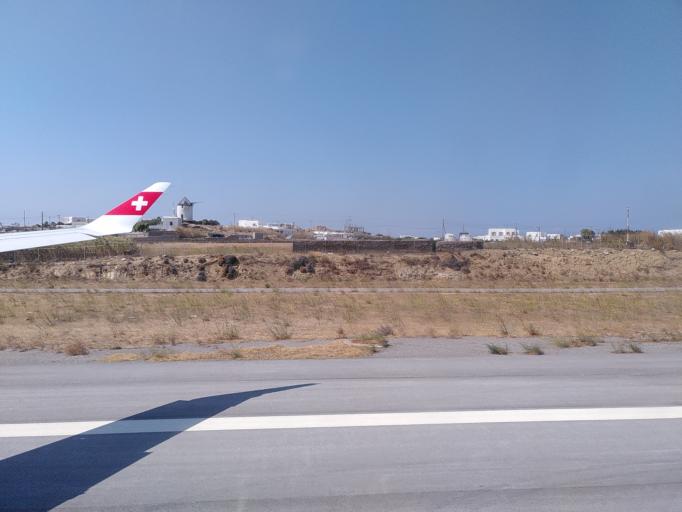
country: GR
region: South Aegean
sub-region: Nomos Kykladon
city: Mykonos
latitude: 37.4327
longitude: 25.3493
